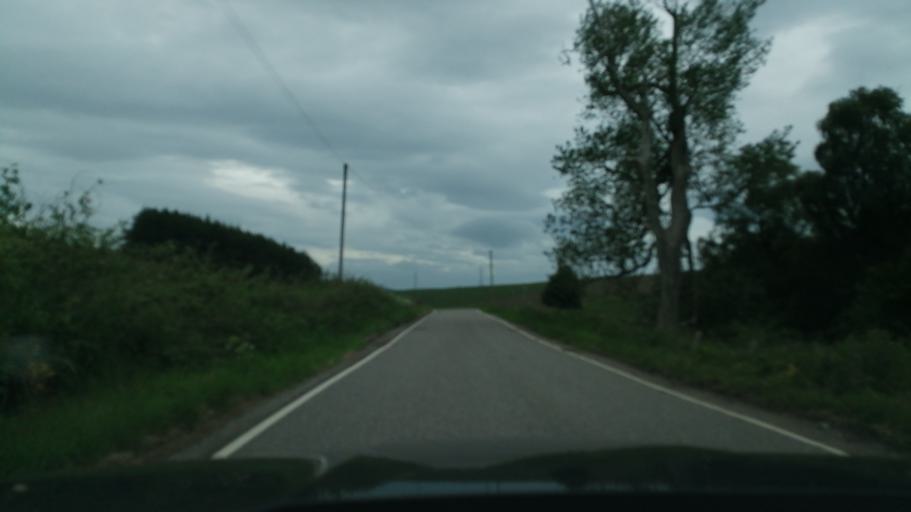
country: GB
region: Scotland
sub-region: Moray
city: Cullen
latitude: 57.6021
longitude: -2.8533
